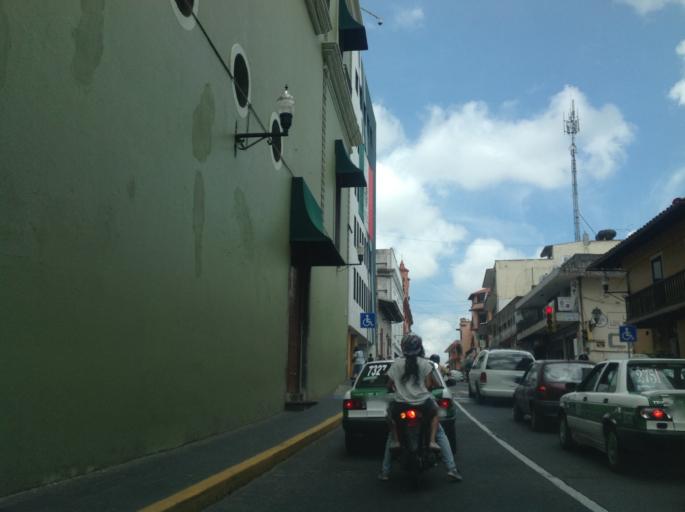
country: MX
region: Veracruz
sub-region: Xalapa
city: Xalapa de Enriquez
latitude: 19.5267
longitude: -96.9222
